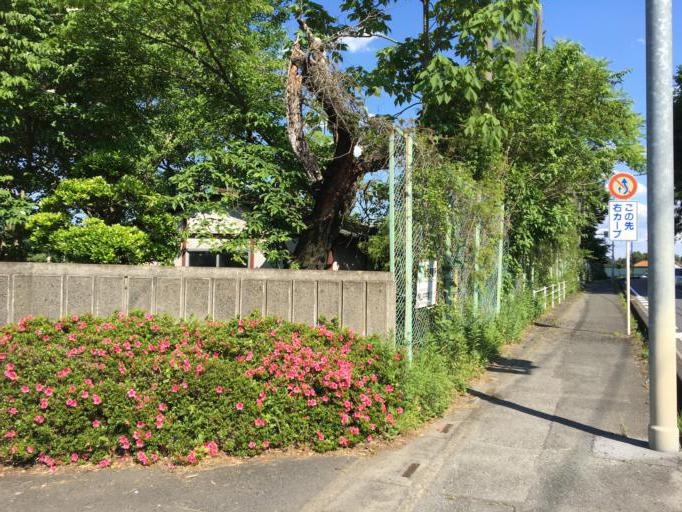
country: JP
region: Saitama
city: Morohongo
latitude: 35.9836
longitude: 139.3334
